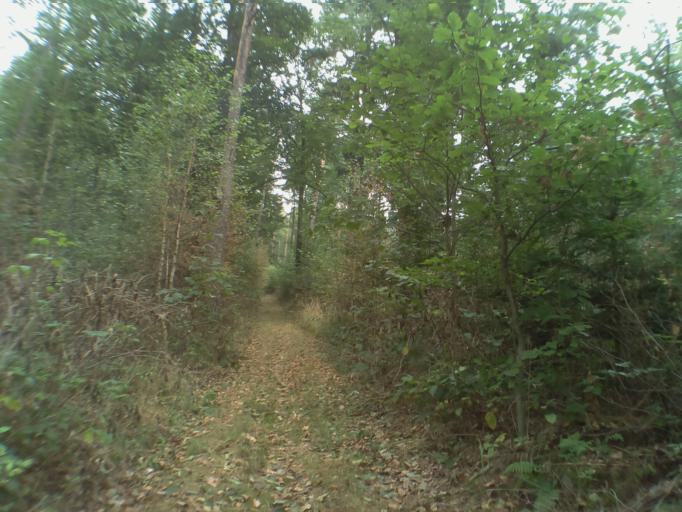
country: PL
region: Lower Silesian Voivodeship
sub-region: Powiat swidnicki
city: Strzegom
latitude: 50.9889
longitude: 16.3102
